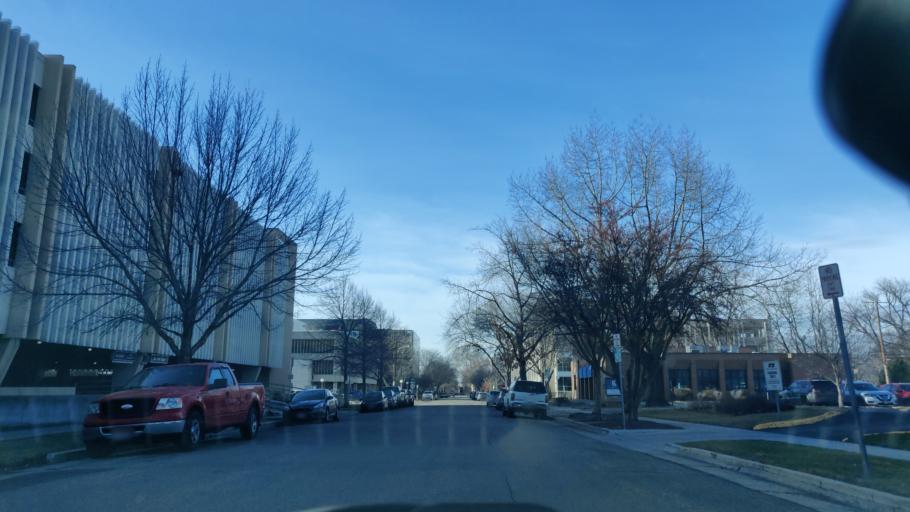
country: US
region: Idaho
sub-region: Ada County
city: Boise
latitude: 43.6178
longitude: -116.1964
